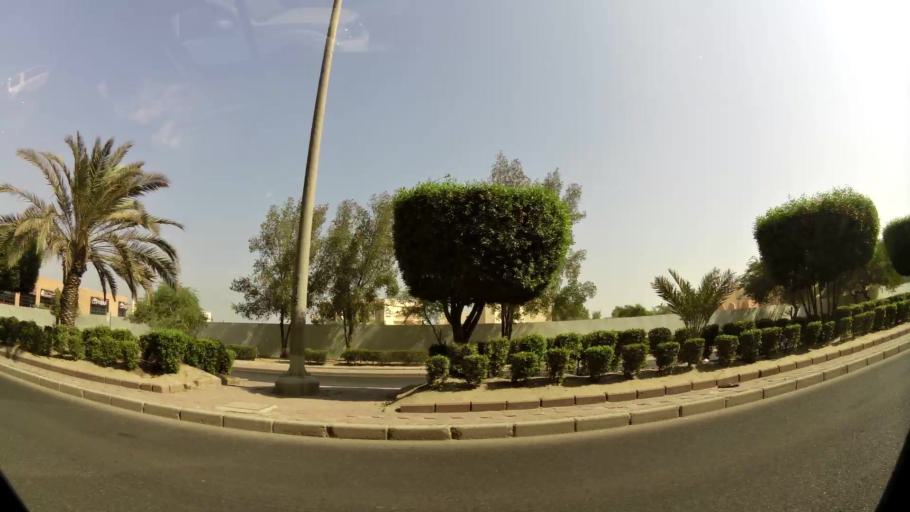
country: KW
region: Al Ahmadi
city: Al Mahbulah
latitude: 29.1528
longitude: 48.1251
